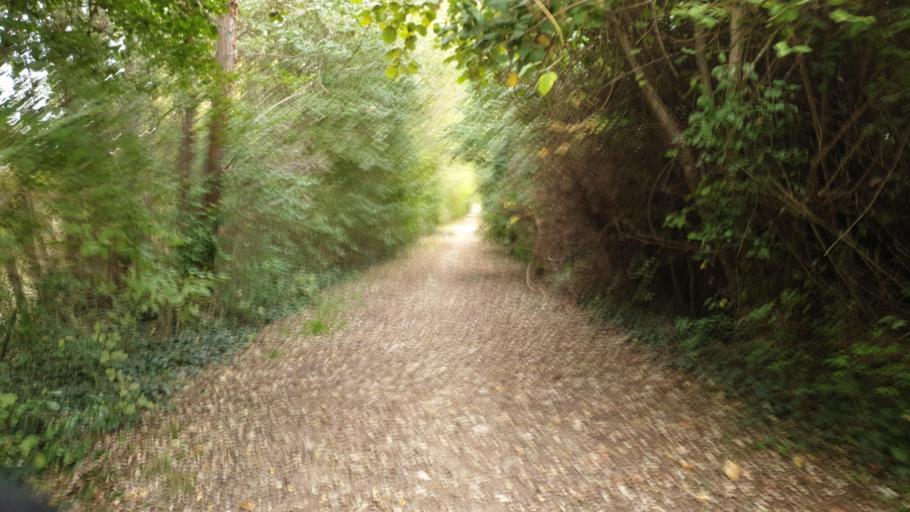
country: IT
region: Veneto
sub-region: Provincia di Padova
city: Villatora
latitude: 45.3818
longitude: 11.9788
